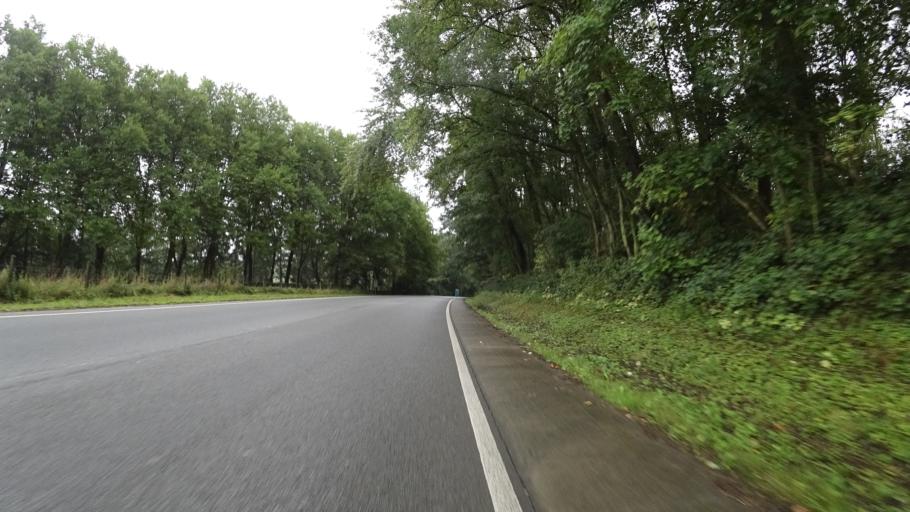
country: BE
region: Wallonia
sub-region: Province de Namur
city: Namur
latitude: 50.4923
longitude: 4.8139
